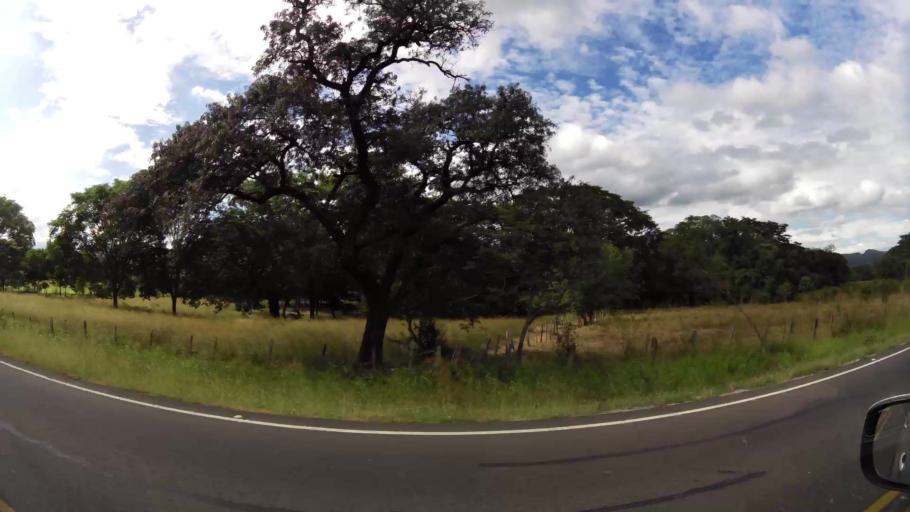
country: CR
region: Guanacaste
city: Hojancha
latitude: 10.1373
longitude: -85.3372
